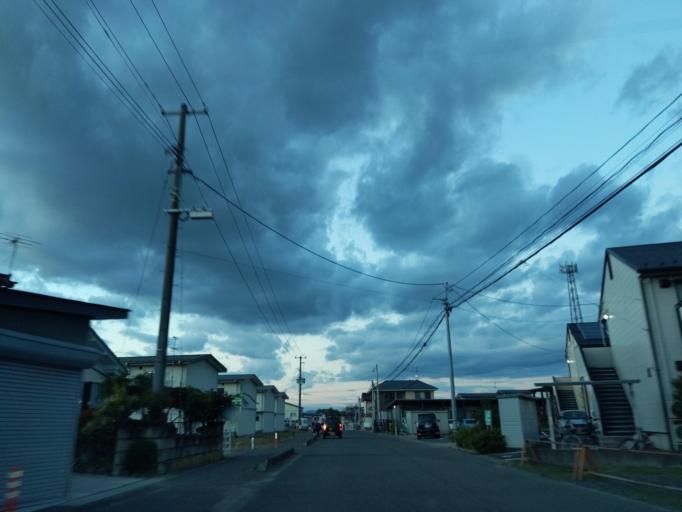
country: JP
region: Fukushima
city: Motomiya
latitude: 37.4951
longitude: 140.3894
